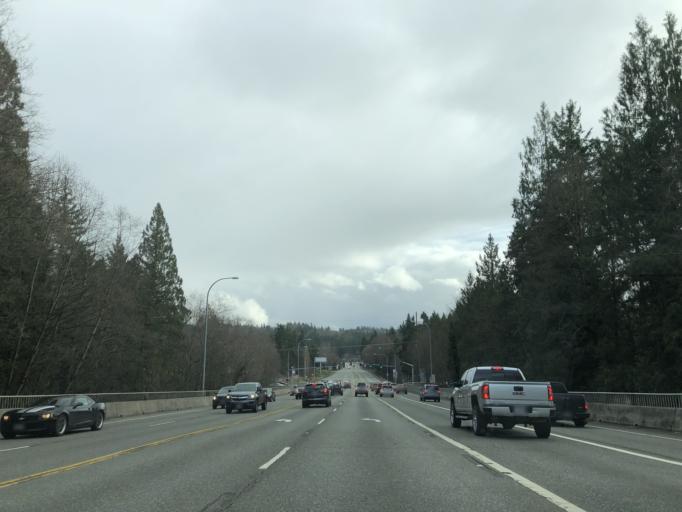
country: US
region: Washington
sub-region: Kitsap County
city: Poulsbo
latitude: 47.7532
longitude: -122.6474
